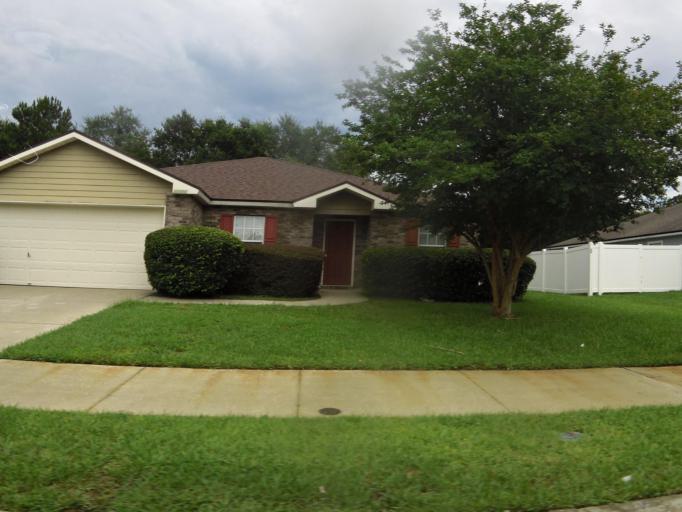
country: US
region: Florida
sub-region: Nassau County
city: Nassau Village-Ratliff
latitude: 30.4414
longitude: -81.7528
